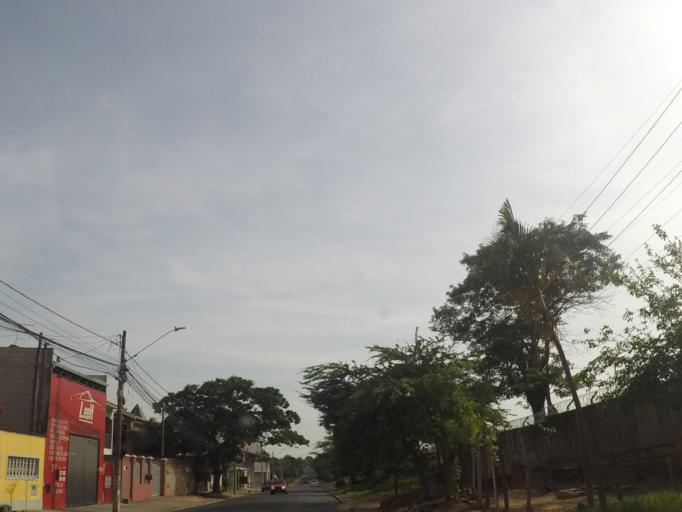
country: BR
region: Sao Paulo
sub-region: Hortolandia
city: Hortolandia
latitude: -22.8599
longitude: -47.1983
